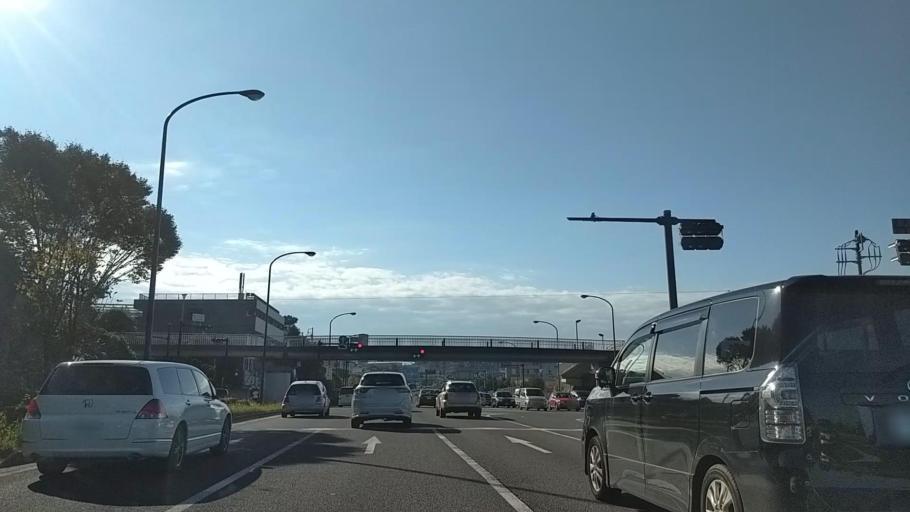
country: JP
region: Kanagawa
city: Yokohama
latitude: 35.4578
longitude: 139.5631
